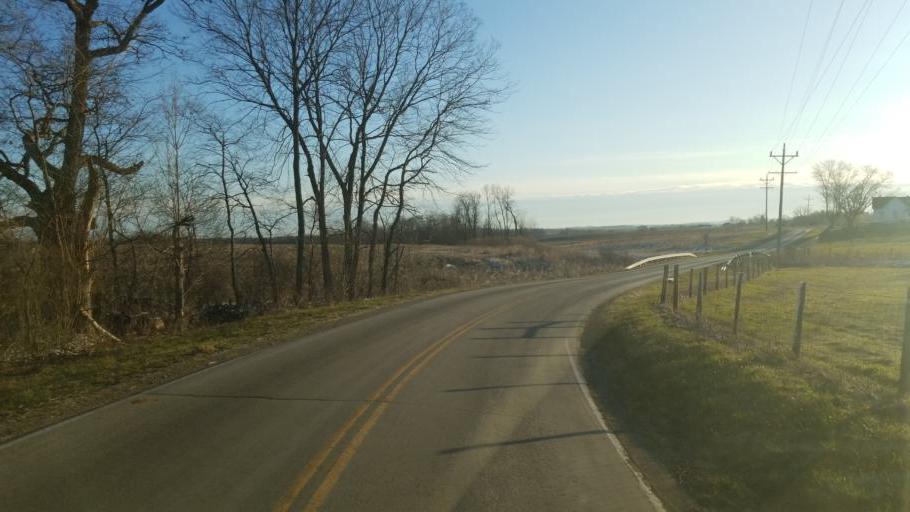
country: US
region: Ohio
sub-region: Highland County
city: Greenfield
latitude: 39.2583
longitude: -83.4622
